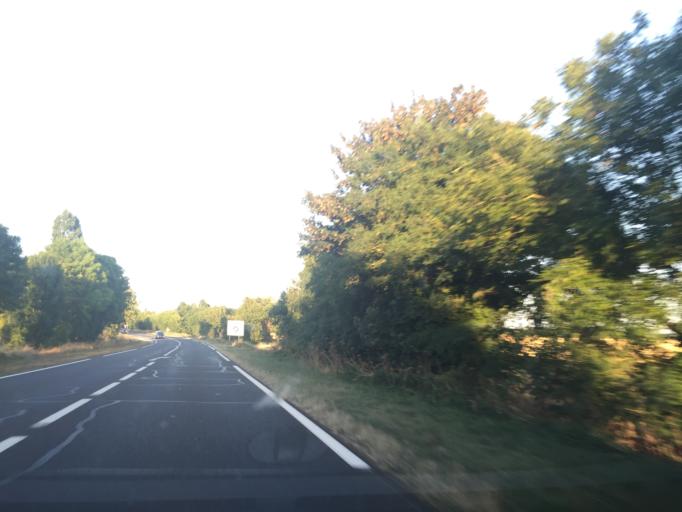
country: FR
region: Poitou-Charentes
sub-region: Departement de la Vienne
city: Lusignan
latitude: 46.4268
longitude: 0.1216
